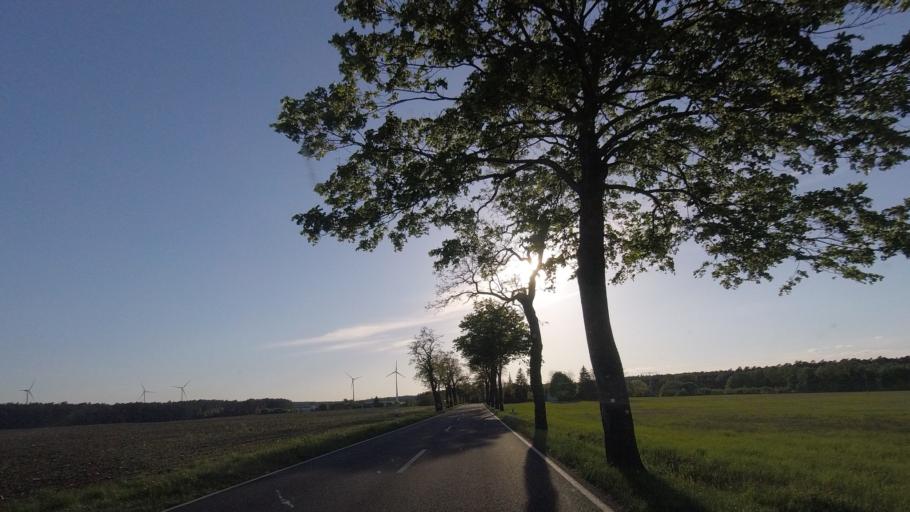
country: DE
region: Brandenburg
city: Ihlow
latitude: 51.9854
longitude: 13.3133
